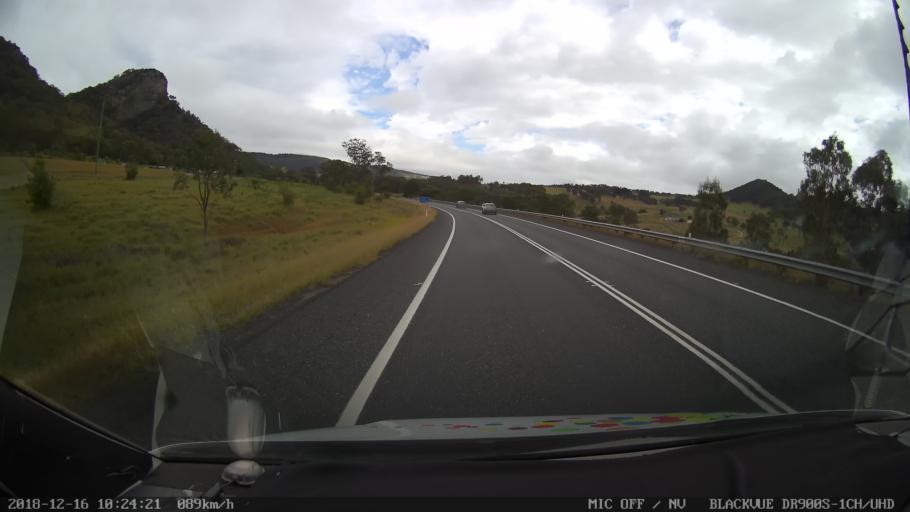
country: AU
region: New South Wales
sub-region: Tenterfield Municipality
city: Carrolls Creek
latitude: -29.1714
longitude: 152.0073
